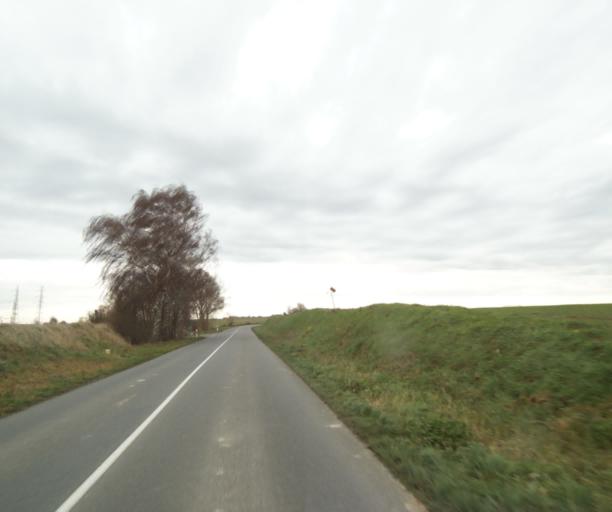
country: FR
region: Nord-Pas-de-Calais
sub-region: Departement du Nord
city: Curgies
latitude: 50.3570
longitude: 3.6005
